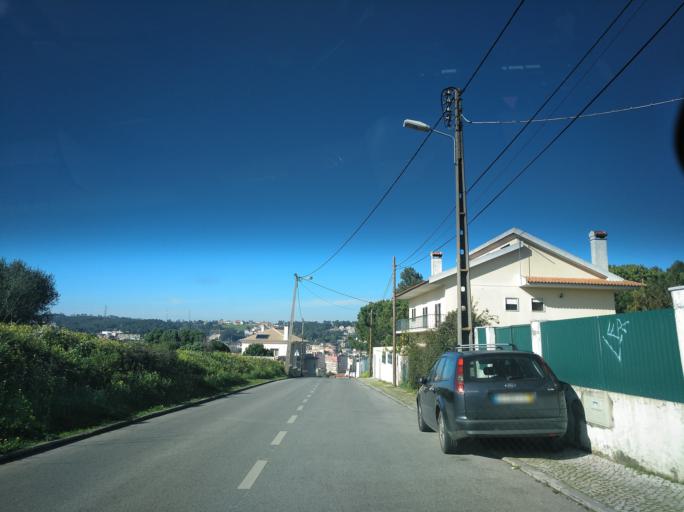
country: PT
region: Lisbon
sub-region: Odivelas
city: Canecas
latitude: 38.8085
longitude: -9.2208
